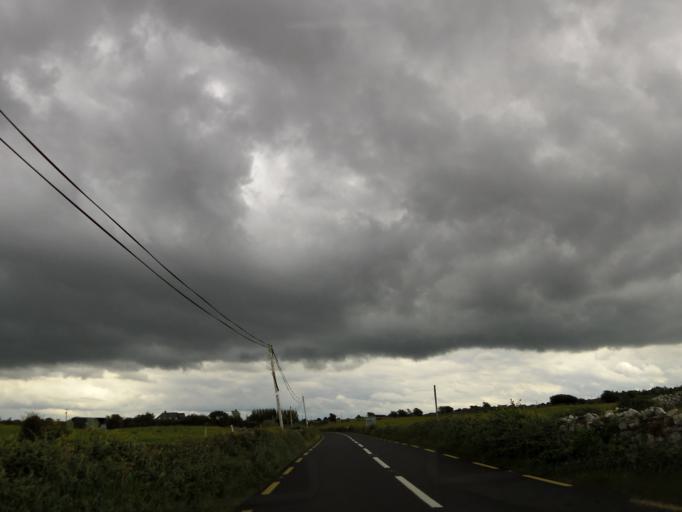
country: IE
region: Connaught
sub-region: County Galway
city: Oranmore
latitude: 53.1440
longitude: -8.9806
